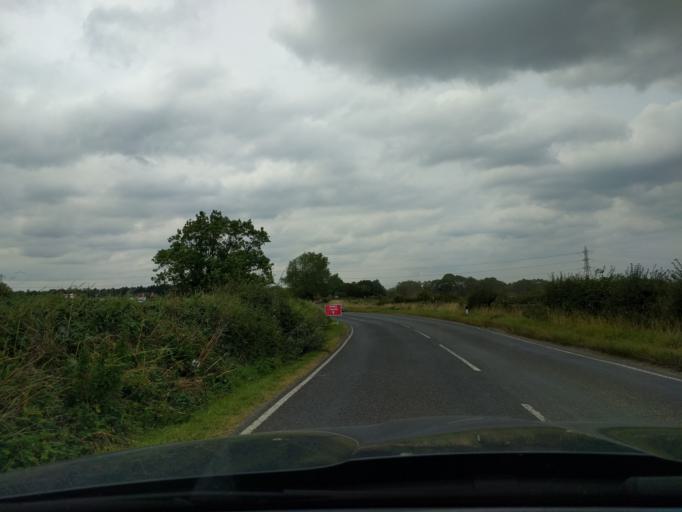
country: GB
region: England
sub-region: Northumberland
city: Stannington
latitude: 55.1328
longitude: -1.6466
